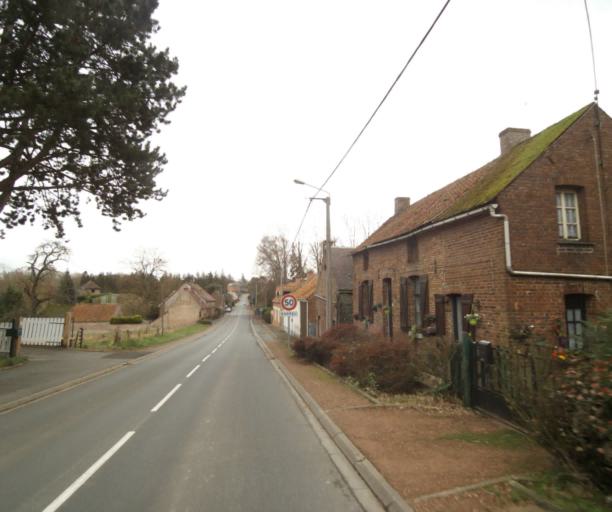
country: FR
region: Nord-Pas-de-Calais
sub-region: Departement du Nord
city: Sebourg
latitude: 50.3349
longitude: 3.6451
